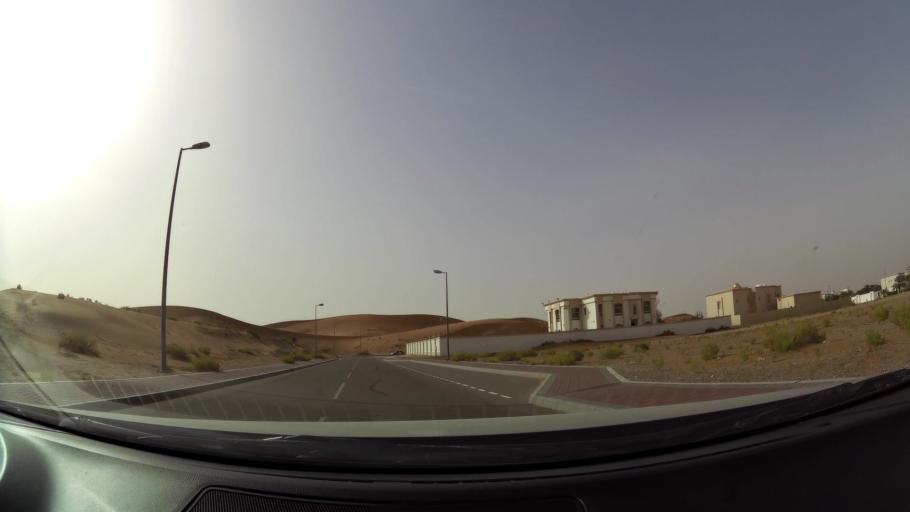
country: AE
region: Abu Dhabi
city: Al Ain
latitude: 24.1971
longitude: 55.6047
